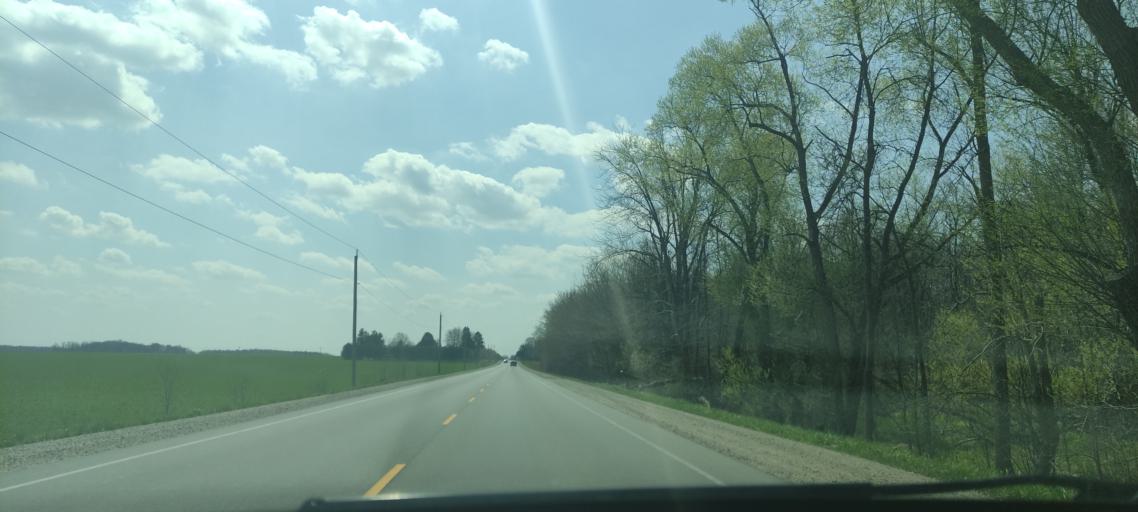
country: CA
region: Ontario
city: Stratford
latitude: 43.3401
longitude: -80.9981
